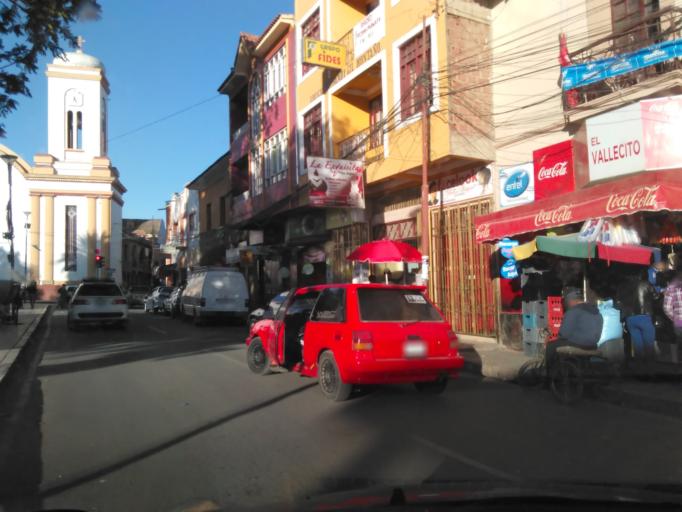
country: BO
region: Cochabamba
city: Punata
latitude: -17.5455
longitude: -65.8366
